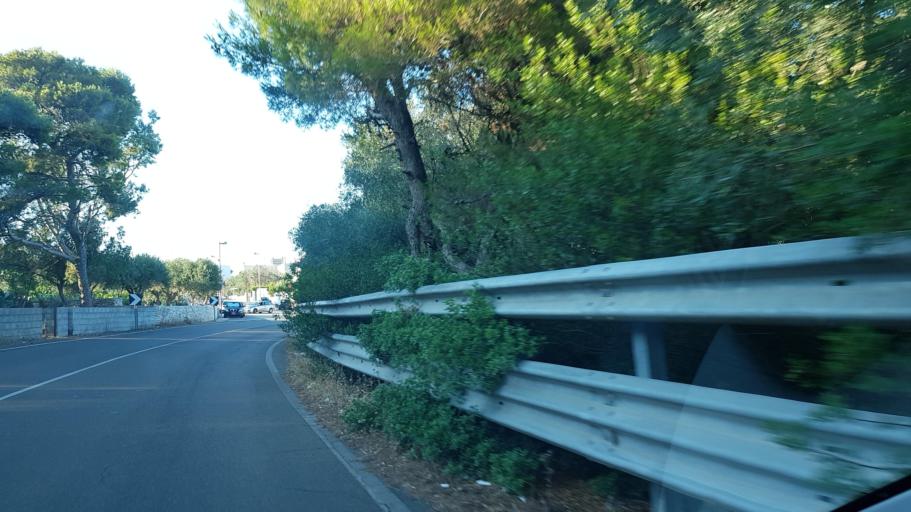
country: IT
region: Apulia
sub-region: Provincia di Lecce
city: Castro
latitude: 40.0016
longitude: 18.4215
